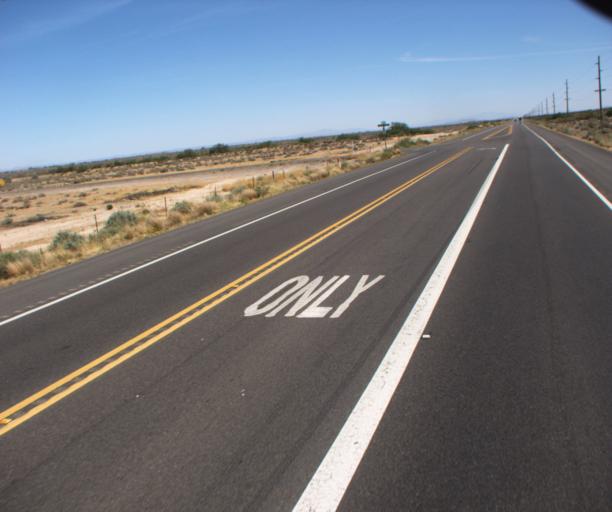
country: US
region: Arizona
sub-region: Pinal County
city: Sacaton
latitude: 33.0496
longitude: -111.6734
